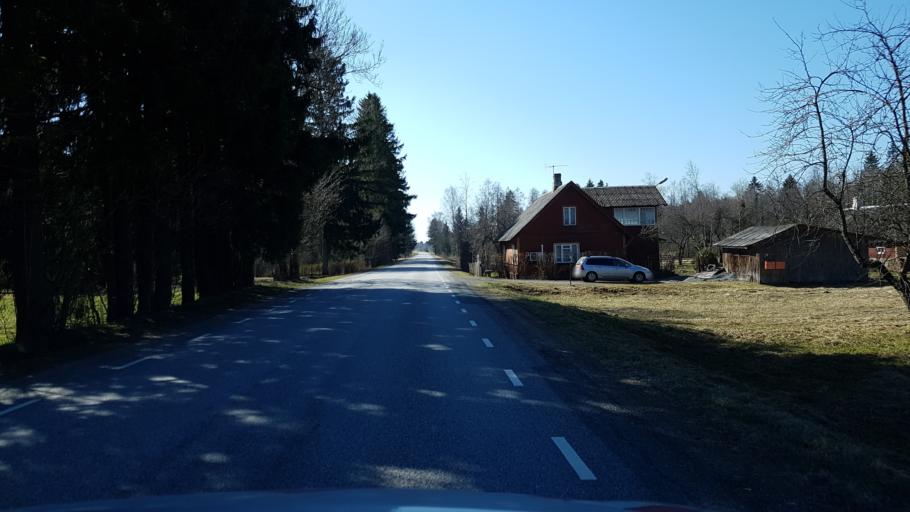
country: EE
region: Ida-Virumaa
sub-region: Kohtla-Nomme vald
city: Kohtla-Nomme
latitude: 59.3016
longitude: 27.2381
